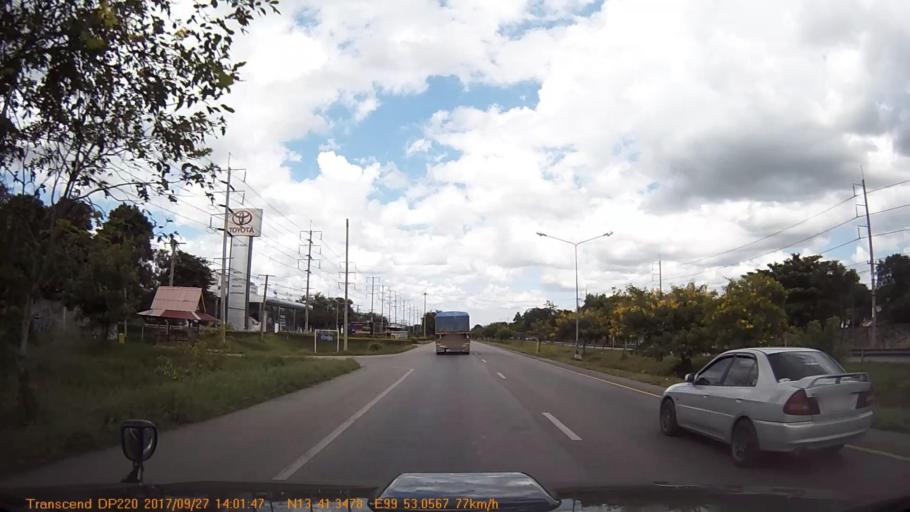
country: TH
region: Ratchaburi
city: Photharam
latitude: 13.6892
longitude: 99.8843
